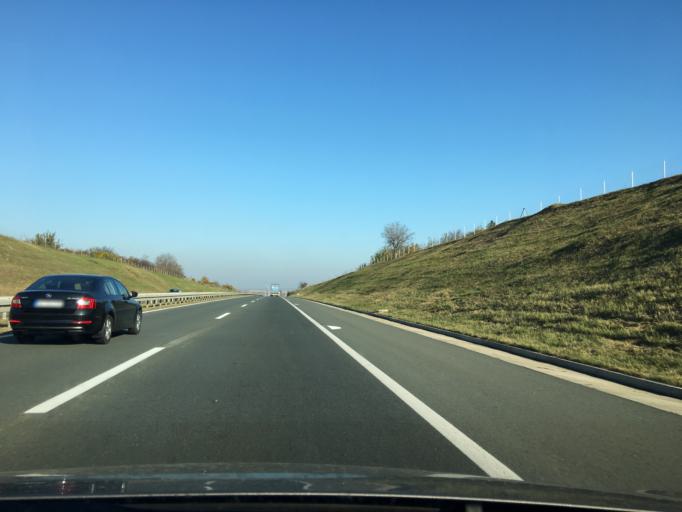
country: RS
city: Beska
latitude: 45.1576
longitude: 20.0818
